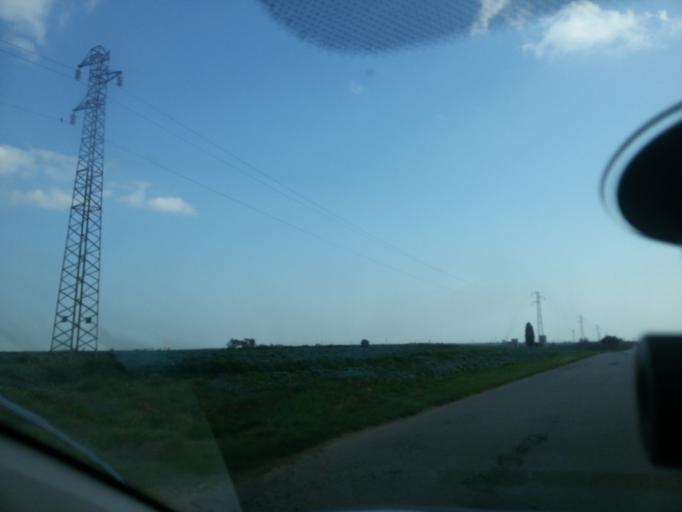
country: IT
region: Apulia
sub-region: Provincia di Brindisi
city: Mesagne
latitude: 40.6366
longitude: 17.8165
